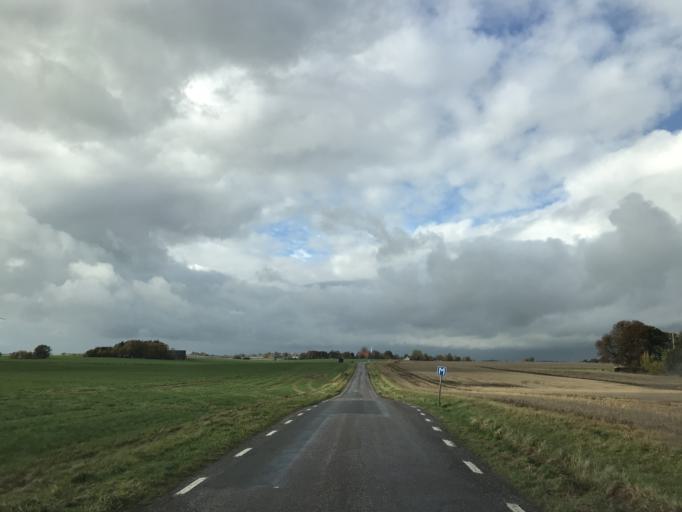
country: SE
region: Skane
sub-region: Svalovs Kommun
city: Svaloev
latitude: 55.9073
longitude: 13.1620
